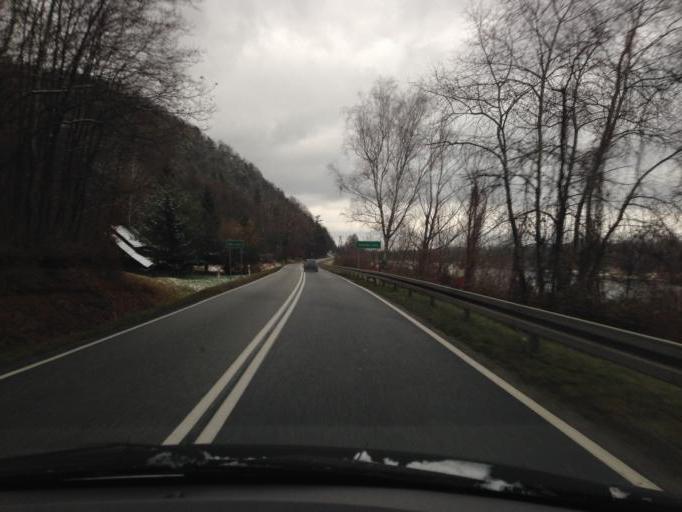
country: PL
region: Lesser Poland Voivodeship
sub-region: Powiat tarnowski
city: Zakliczyn
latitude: 49.8674
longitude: 20.7885
